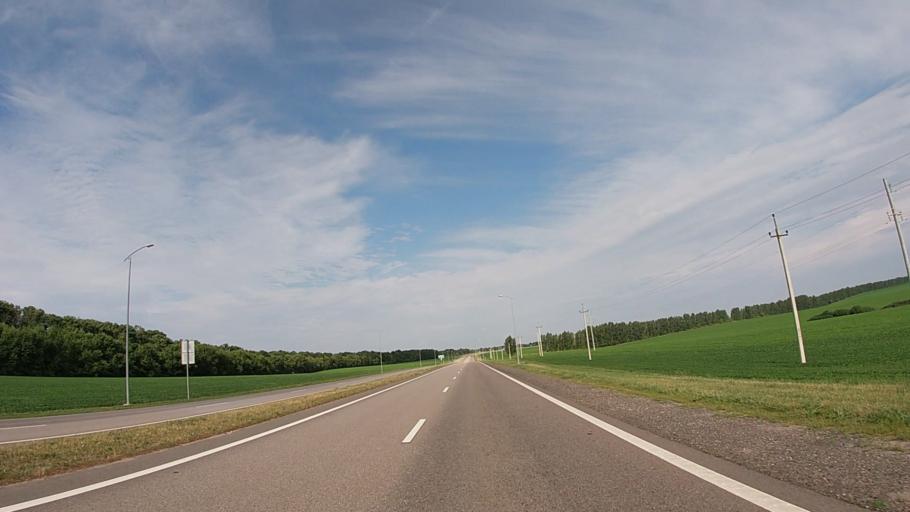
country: RU
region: Belgorod
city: Rakitnoye
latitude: 50.7905
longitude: 35.8834
